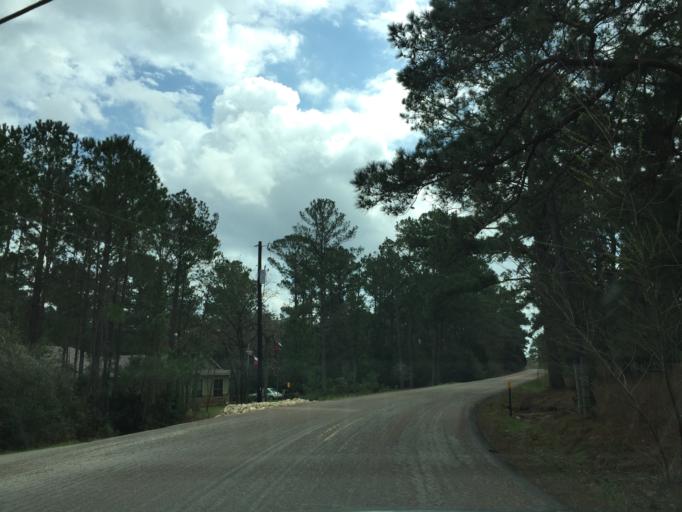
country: US
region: Texas
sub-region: Bastrop County
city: Bastrop
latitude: 30.1260
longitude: -97.2801
